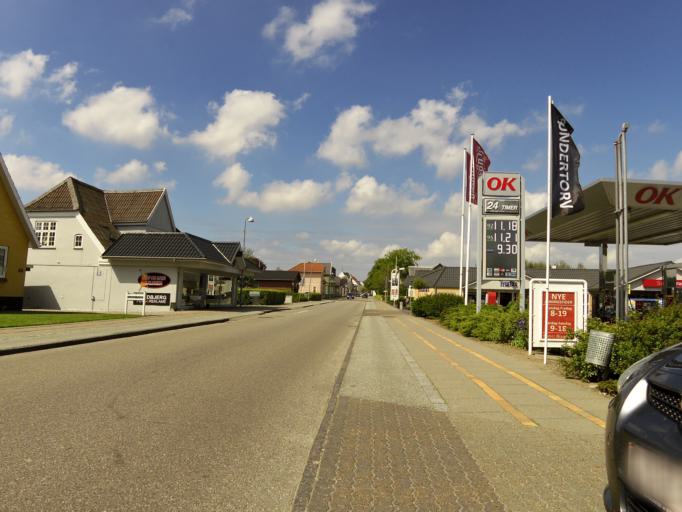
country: DK
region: South Denmark
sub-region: Tonder Kommune
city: Toftlund
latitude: 55.1889
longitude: 9.0652
